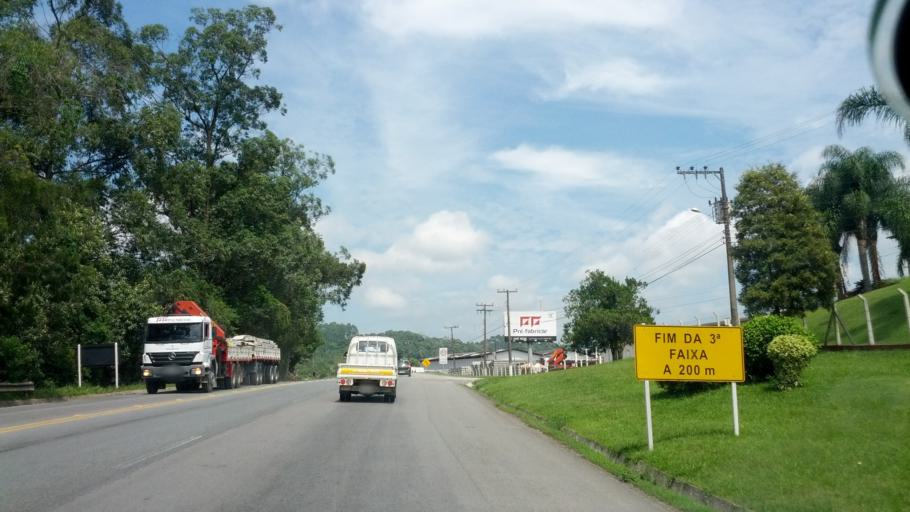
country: BR
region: Santa Catarina
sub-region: Ibirama
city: Ibirama
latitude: -27.1069
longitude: -49.5223
